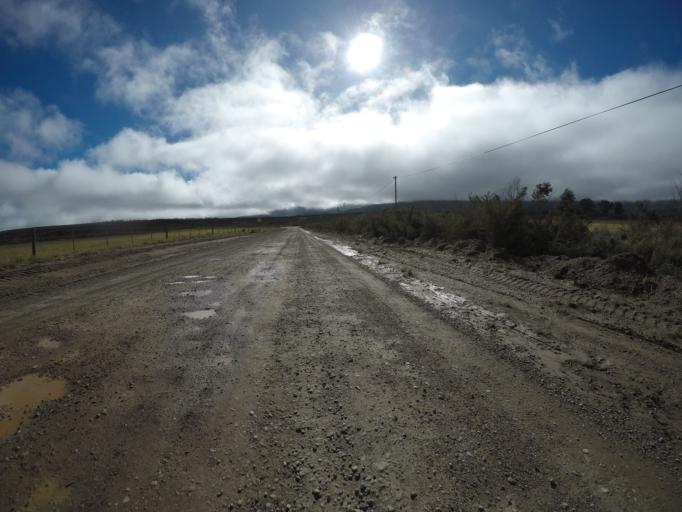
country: ZA
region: Western Cape
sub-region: Cape Winelands District Municipality
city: Ashton
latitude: -34.1236
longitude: 19.8391
